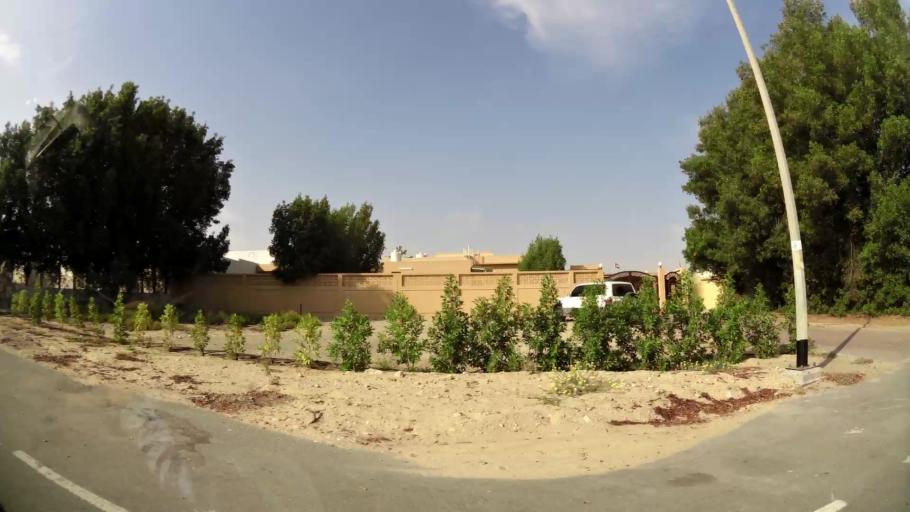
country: AE
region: Ash Shariqah
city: Sharjah
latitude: 25.2167
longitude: 55.3913
